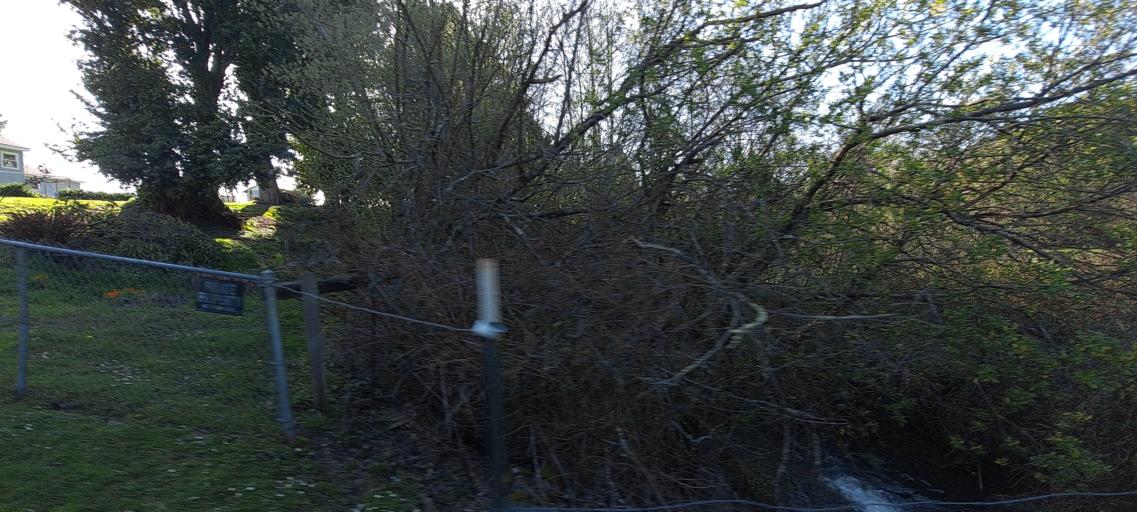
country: US
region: California
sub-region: Humboldt County
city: Fortuna
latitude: 40.5745
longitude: -124.1383
